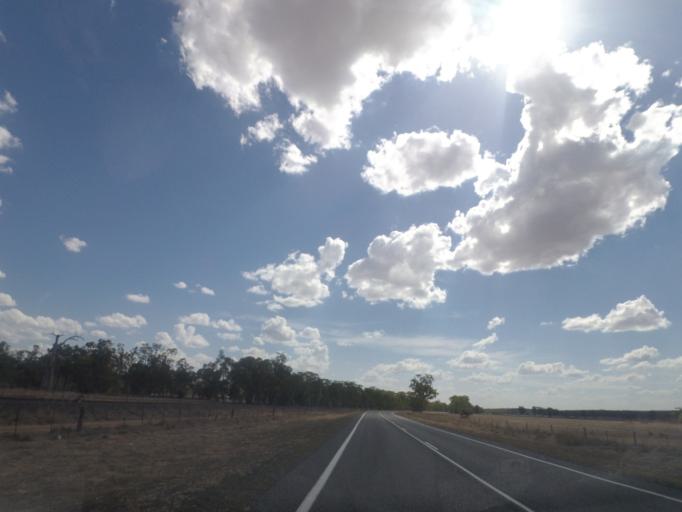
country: AU
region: Queensland
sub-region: Southern Downs
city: Stanthorpe
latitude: -28.3935
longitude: 151.3152
